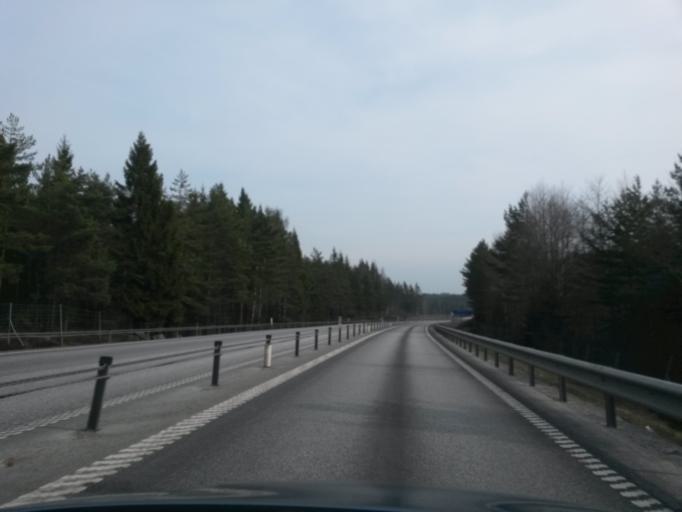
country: SE
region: OErebro
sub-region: Laxa Kommun
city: Laxa
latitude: 58.9561
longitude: 14.5108
